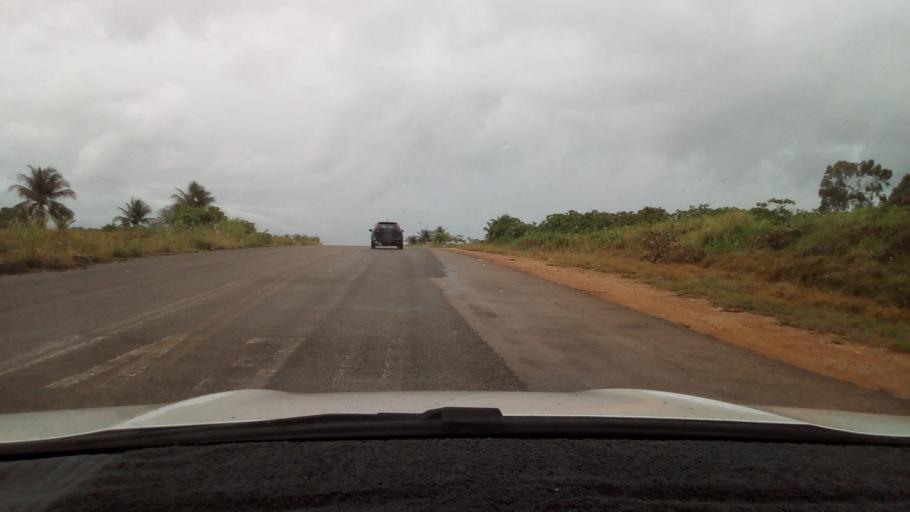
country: BR
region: Paraiba
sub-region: Pitimbu
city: Pitimbu
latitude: -7.4218
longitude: -34.8328
